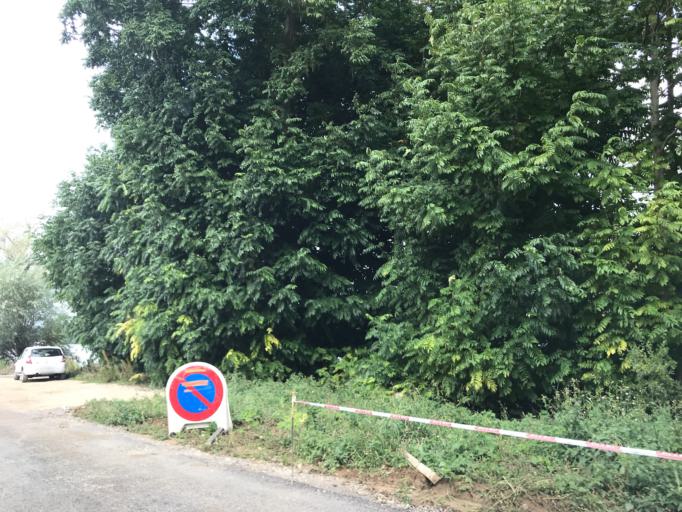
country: FR
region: Haute-Normandie
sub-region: Departement de l'Eure
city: Vernon
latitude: 49.1006
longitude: 1.4743
